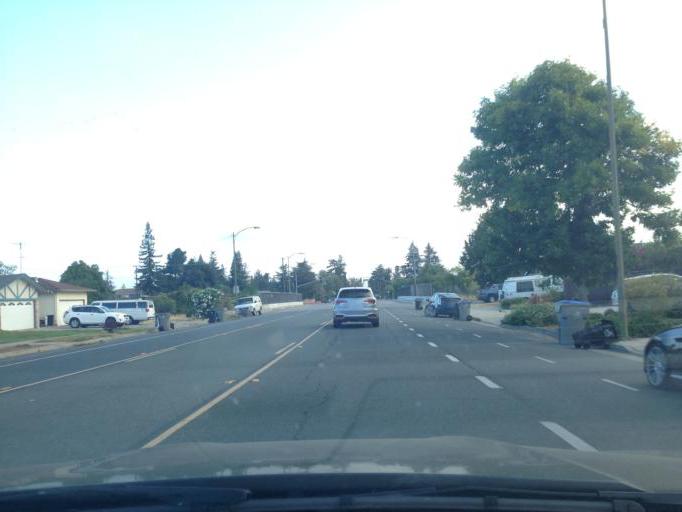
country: US
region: California
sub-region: Santa Clara County
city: Cambrian Park
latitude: 37.2493
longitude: -121.9222
